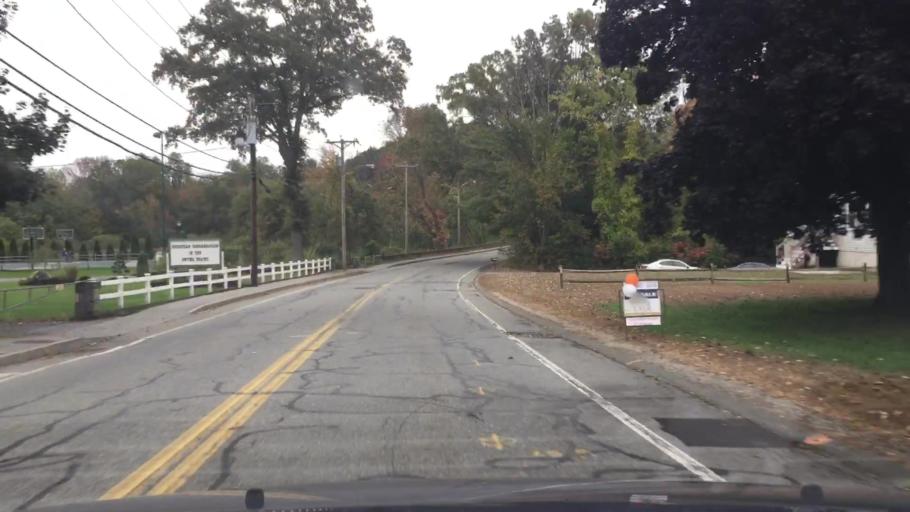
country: US
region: Massachusetts
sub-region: Middlesex County
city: Dracut
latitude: 42.6790
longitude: -71.3614
